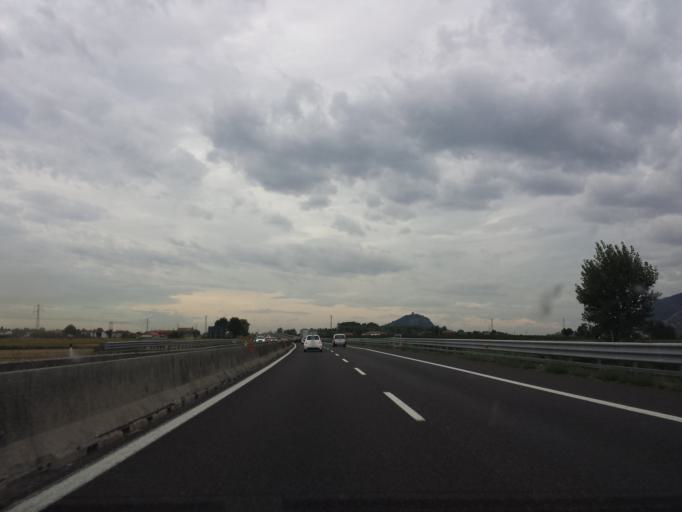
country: IT
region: Veneto
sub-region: Provincia di Padova
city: Battaglia Terme
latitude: 45.2722
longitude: 11.7848
